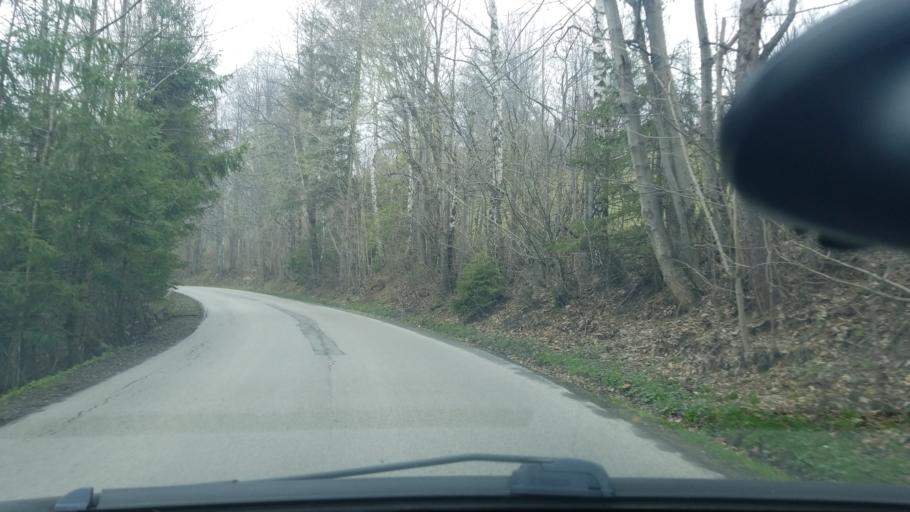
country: PL
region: Silesian Voivodeship
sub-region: Powiat cieszynski
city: Ustron
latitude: 49.7150
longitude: 18.8496
